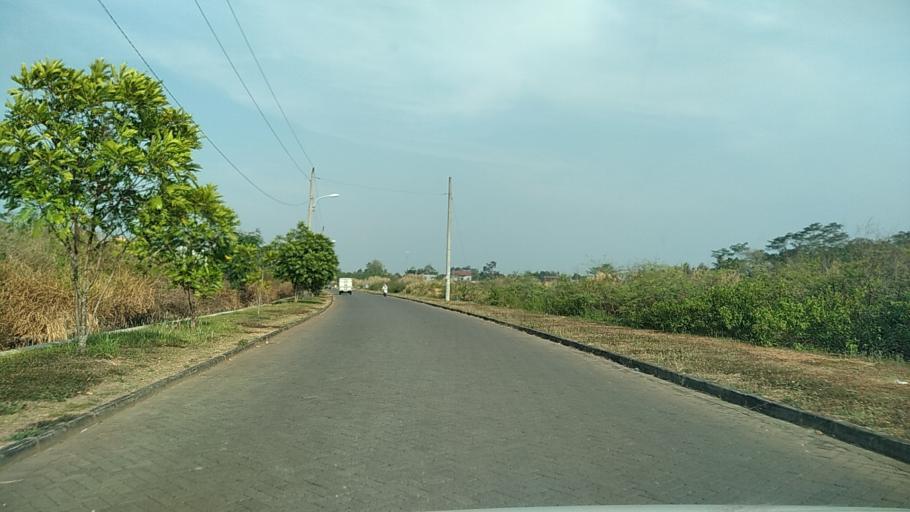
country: ID
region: Central Java
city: Semarang
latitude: -7.0519
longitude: 110.3226
